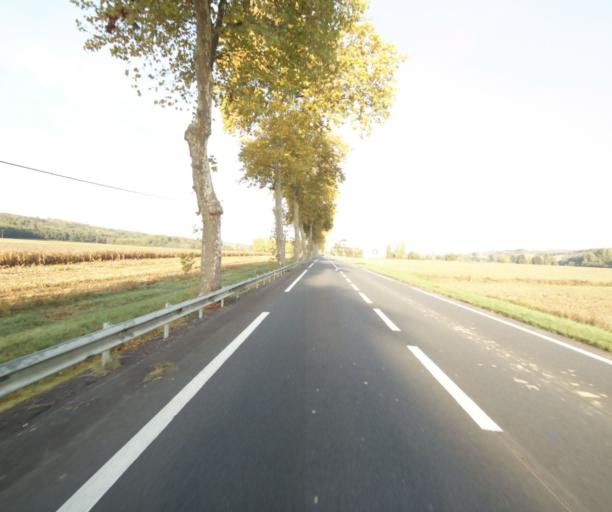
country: FR
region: Midi-Pyrenees
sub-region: Departement du Tarn-et-Garonne
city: Saint-Nauphary
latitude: 43.9426
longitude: 1.4673
